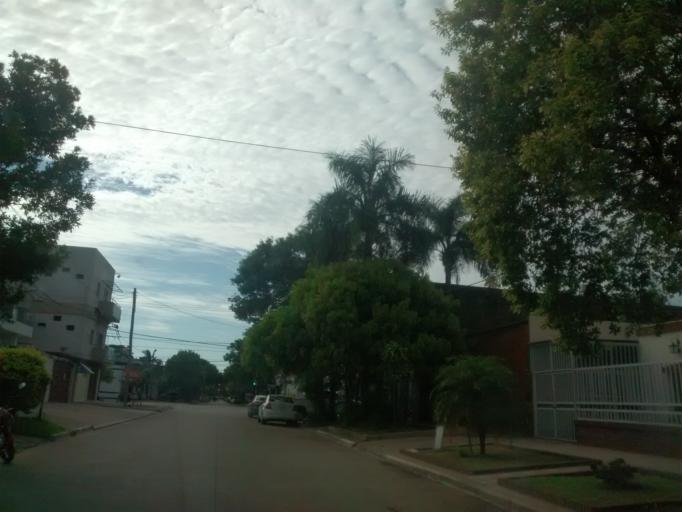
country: AR
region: Chaco
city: Resistencia
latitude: -27.4427
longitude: -58.9782
